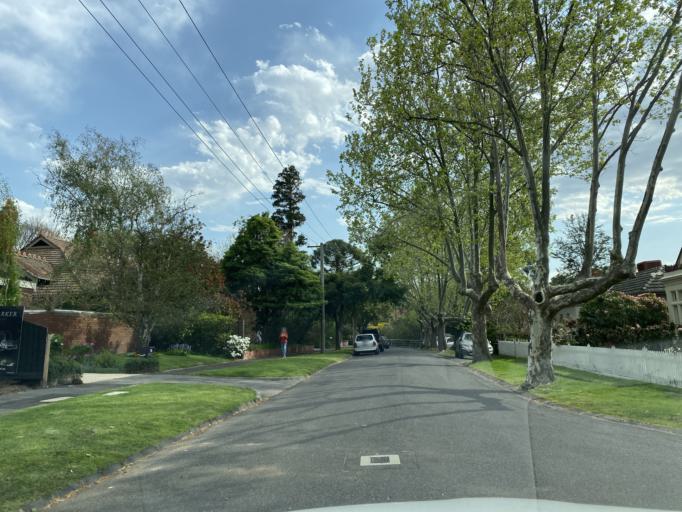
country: AU
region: Victoria
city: Balwyn
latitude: -37.8276
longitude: 145.0690
